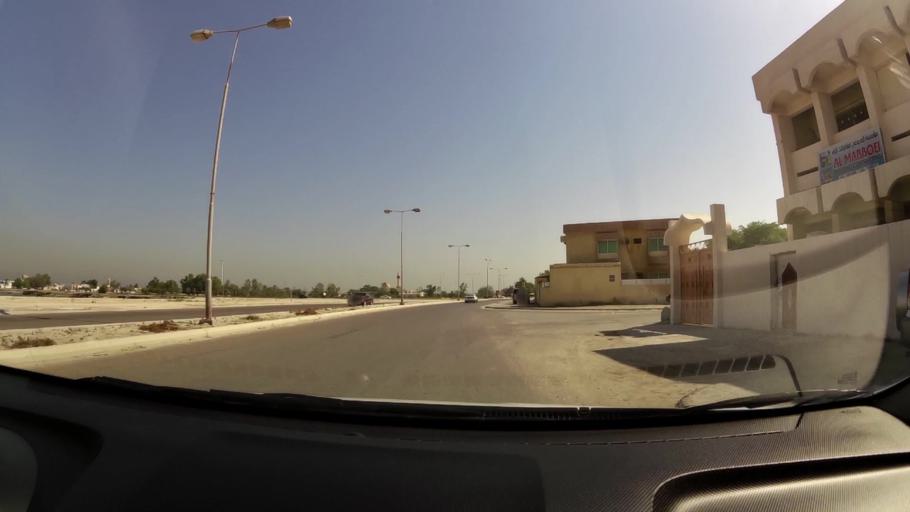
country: AE
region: Umm al Qaywayn
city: Umm al Qaywayn
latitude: 25.5832
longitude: 55.5683
